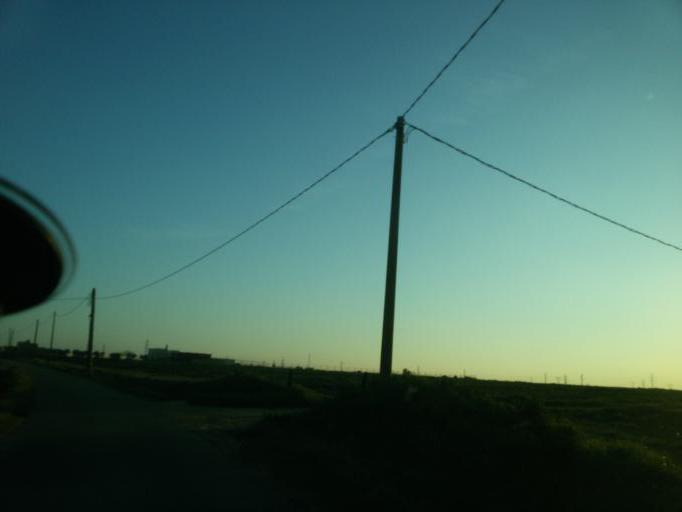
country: IT
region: Apulia
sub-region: Provincia di Brindisi
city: La Rosa
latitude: 40.6082
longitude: 17.9381
